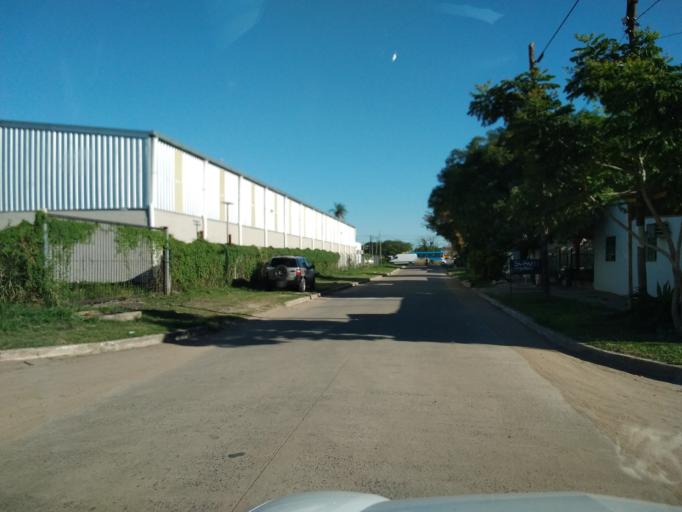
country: AR
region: Corrientes
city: Corrientes
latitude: -27.4749
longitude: -58.7924
